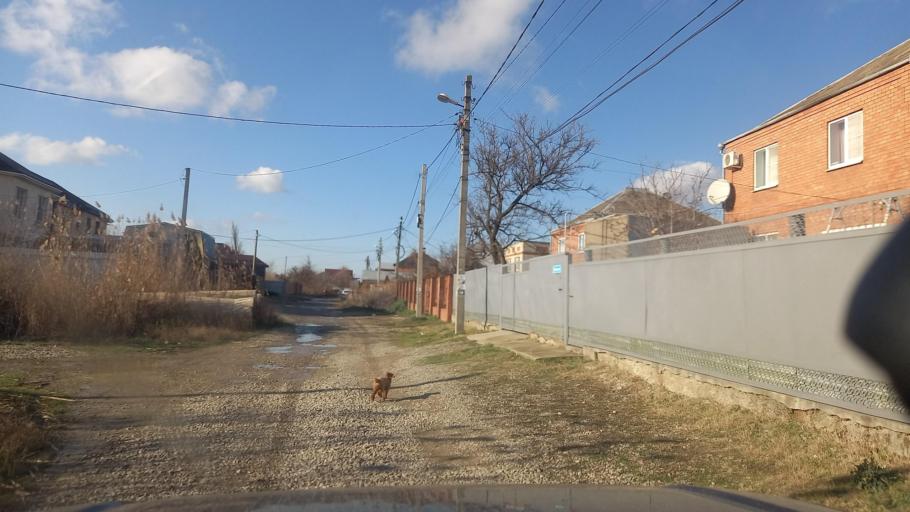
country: RU
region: Adygeya
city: Yablonovskiy
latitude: 44.9922
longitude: 38.9447
